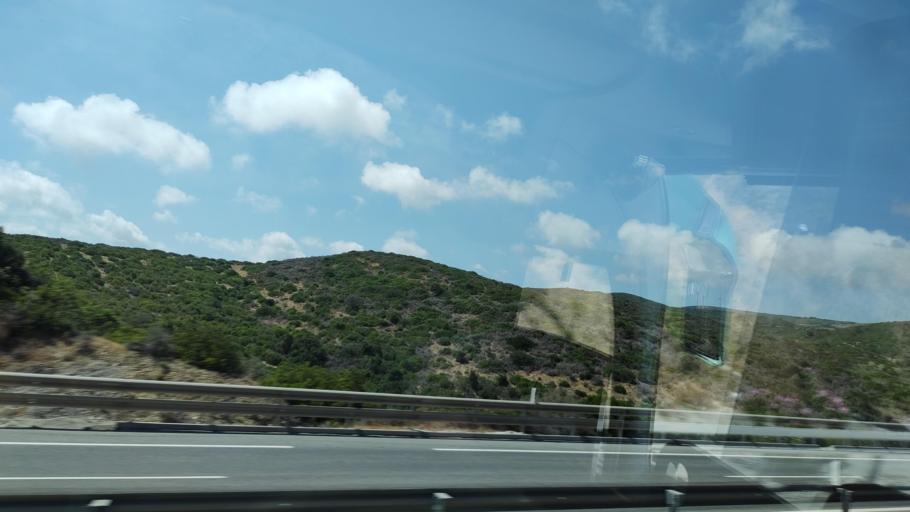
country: ES
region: Andalusia
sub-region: Provincia de Malaga
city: Manilva
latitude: 36.3541
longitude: -5.2701
